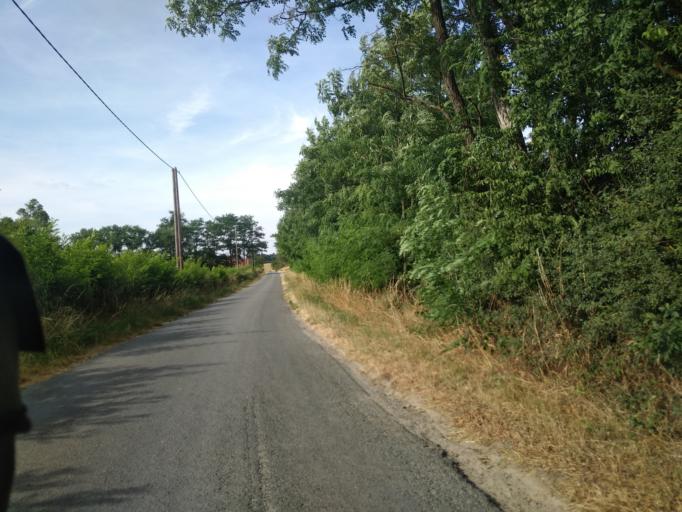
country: FR
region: Bourgogne
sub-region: Departement de Saone-et-Loire
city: Bourbon-Lancy
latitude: 46.6680
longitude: 3.7601
